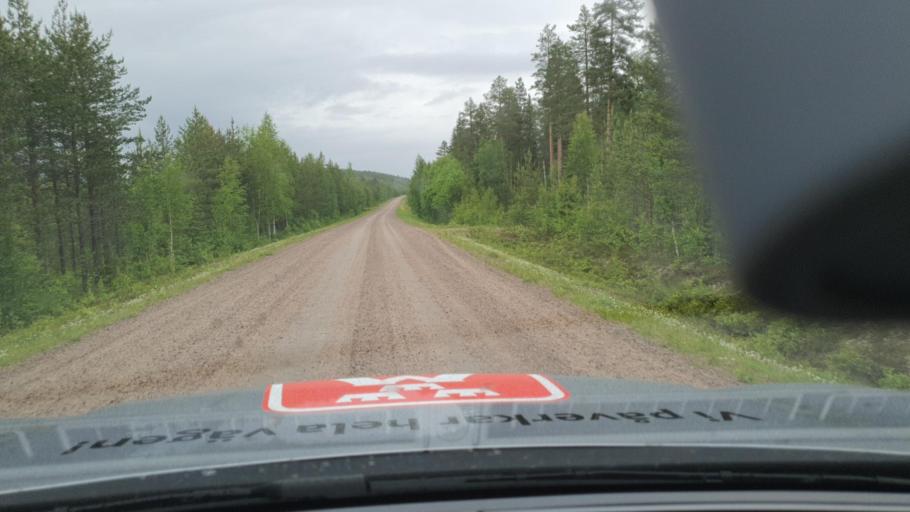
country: SE
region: Norrbotten
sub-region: Overkalix Kommun
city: OEverkalix
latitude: 66.5797
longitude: 22.7450
